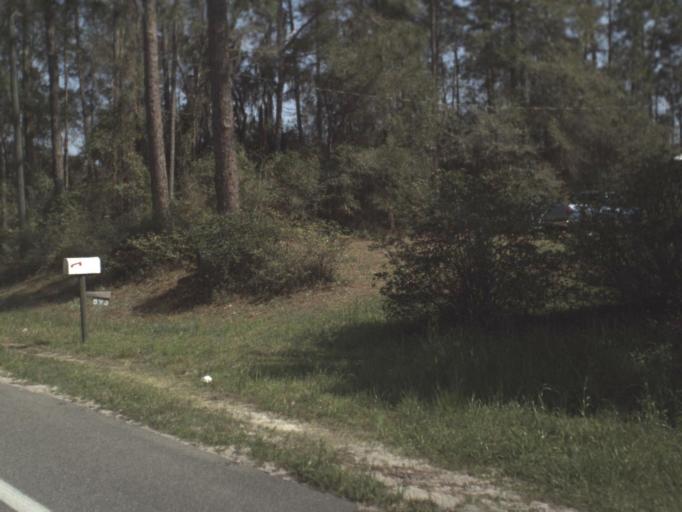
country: US
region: Florida
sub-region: Wakulla County
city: Crawfordville
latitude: 30.0757
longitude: -84.4301
